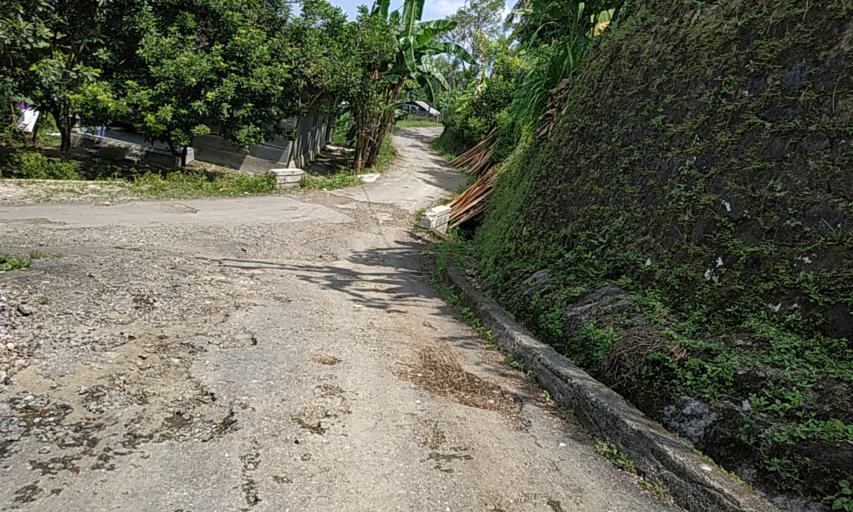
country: ID
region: Central Java
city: Kutoarjo
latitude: -7.6226
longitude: 109.7260
